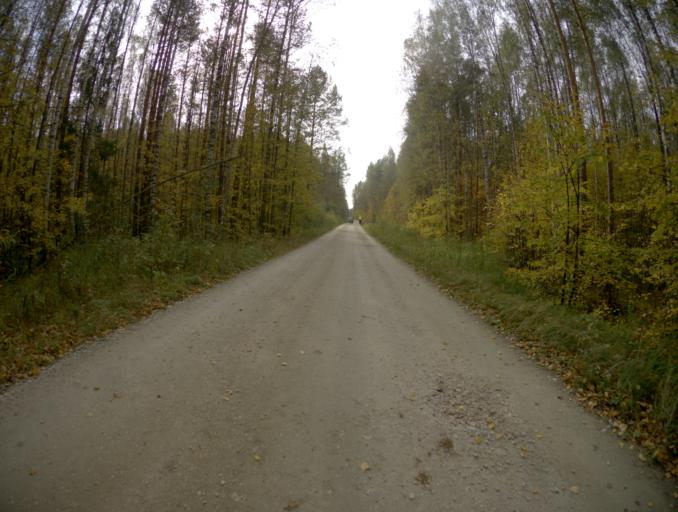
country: RU
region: Ivanovo
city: Lezhnevo
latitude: 56.5548
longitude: 40.7700
